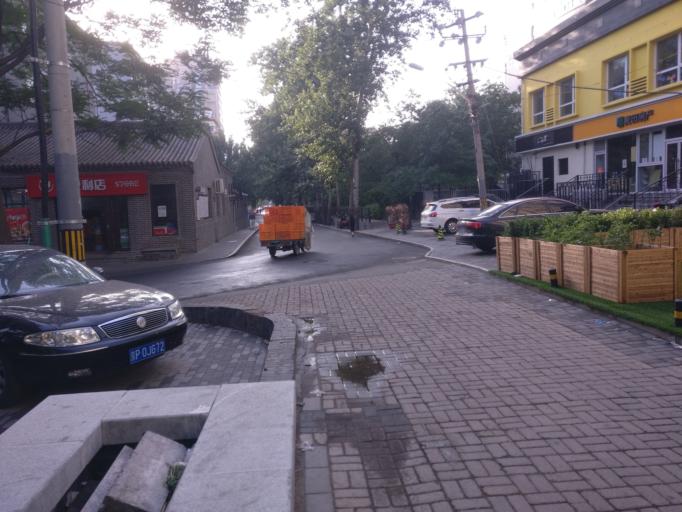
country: CN
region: Beijing
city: Chaowai
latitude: 39.9350
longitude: 116.4346
